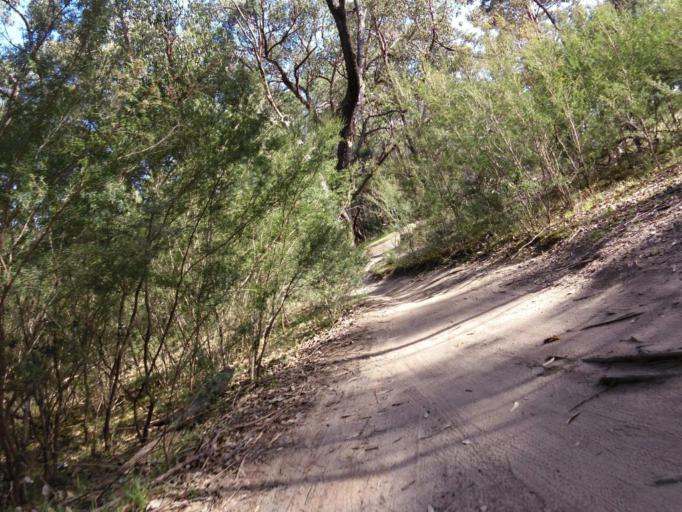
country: AU
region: Victoria
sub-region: Yarra Ranges
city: Lysterfield
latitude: -37.9356
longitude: 145.2994
